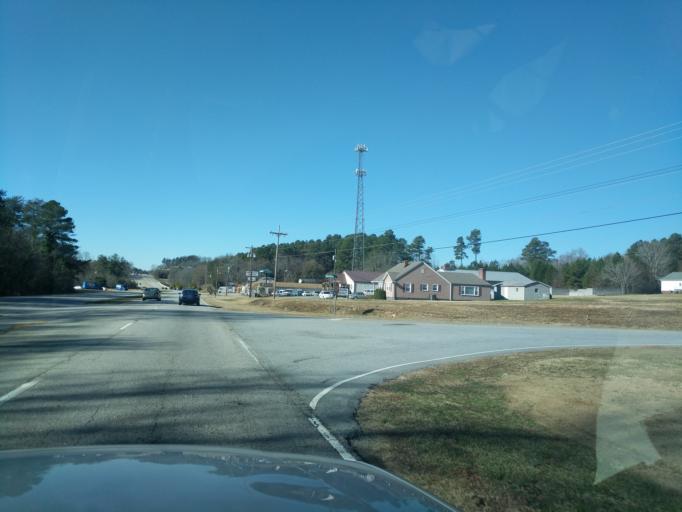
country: US
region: South Carolina
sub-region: Greenville County
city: Parker
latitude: 34.8329
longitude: -82.4786
